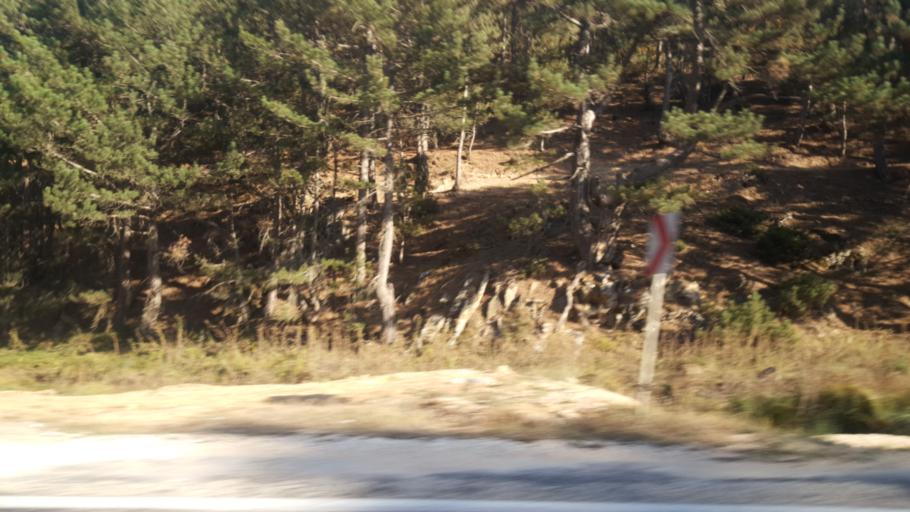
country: TR
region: Afyonkarahisar
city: Ihsaniye
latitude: 39.1047
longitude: 30.5813
